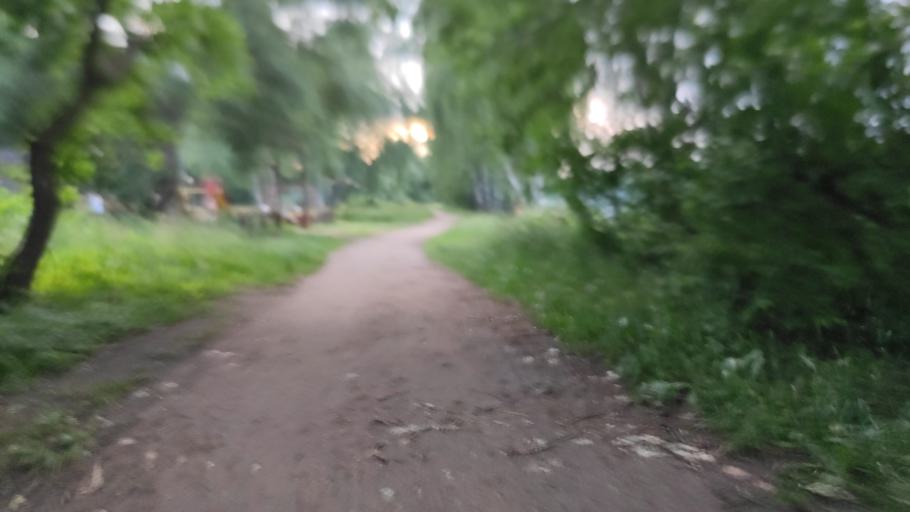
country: BY
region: Minsk
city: Zhdanovichy
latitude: 53.9623
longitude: 27.4444
